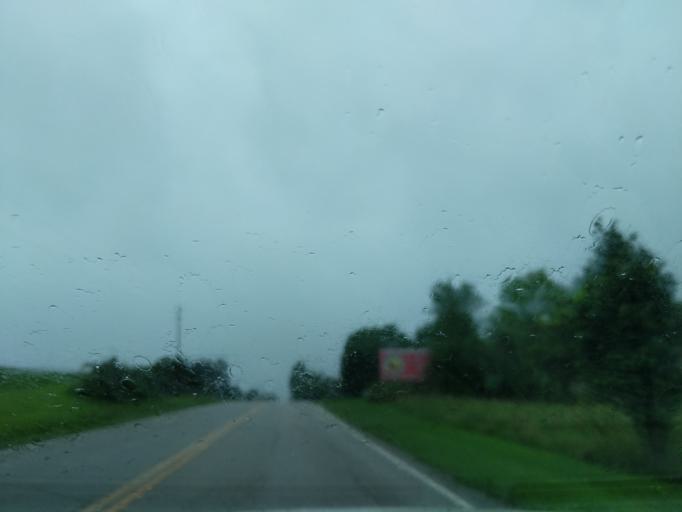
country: US
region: Kentucky
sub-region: Barren County
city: Cave City
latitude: 37.1319
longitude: -86.0459
